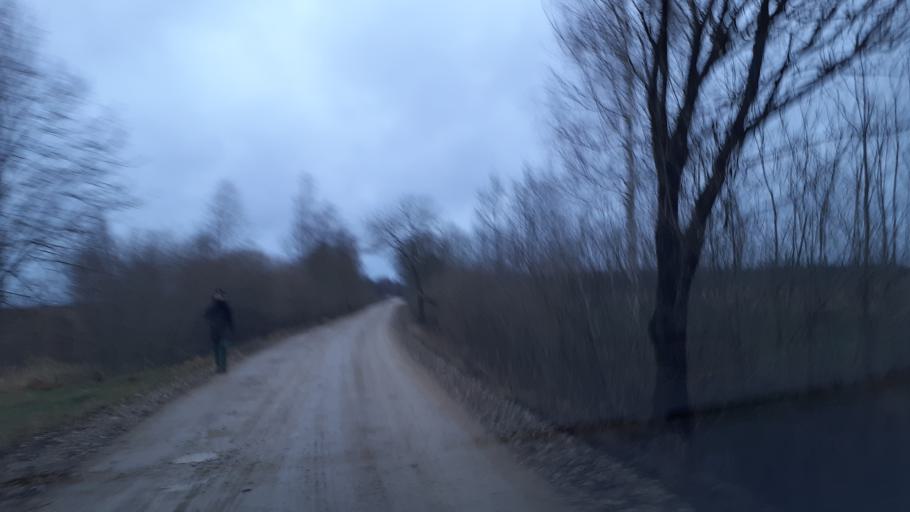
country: LV
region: Kuldigas Rajons
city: Kuldiga
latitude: 57.0445
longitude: 22.1342
